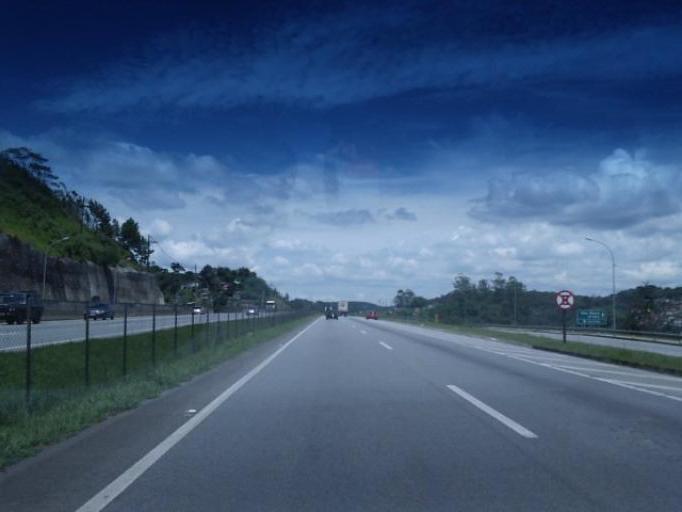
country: BR
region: Sao Paulo
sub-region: Juquitiba
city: Juquitiba
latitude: -23.9365
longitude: -47.0671
